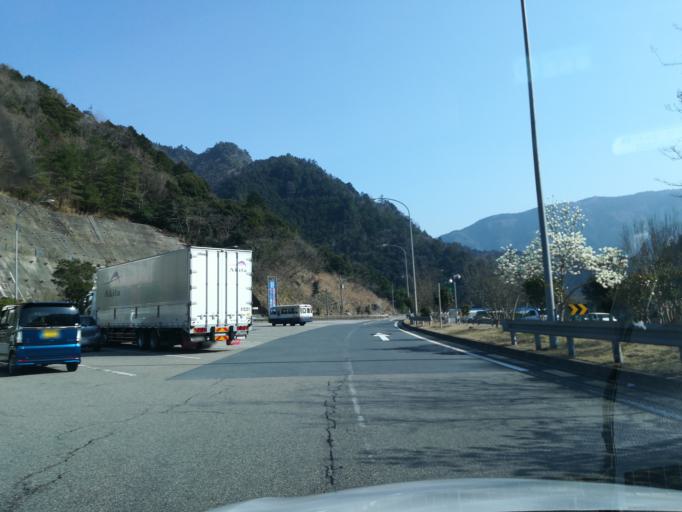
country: JP
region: Ehime
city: Kawanoecho
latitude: 33.9108
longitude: 133.6303
